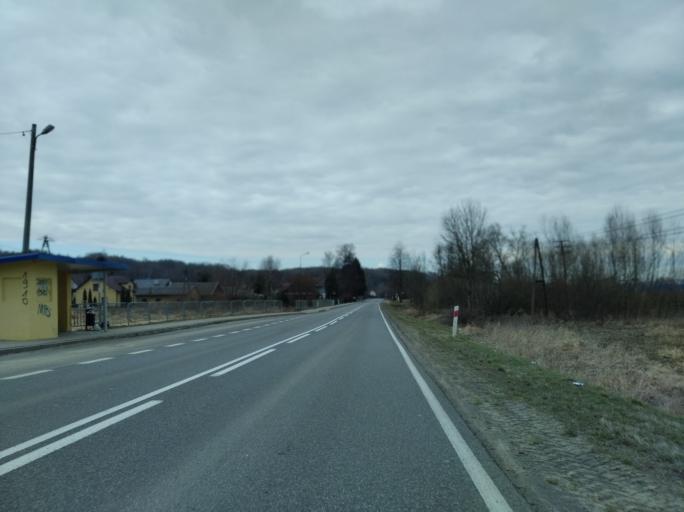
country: PL
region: Subcarpathian Voivodeship
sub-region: Powiat krosnienski
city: Leki
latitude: 49.7980
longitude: 21.6479
